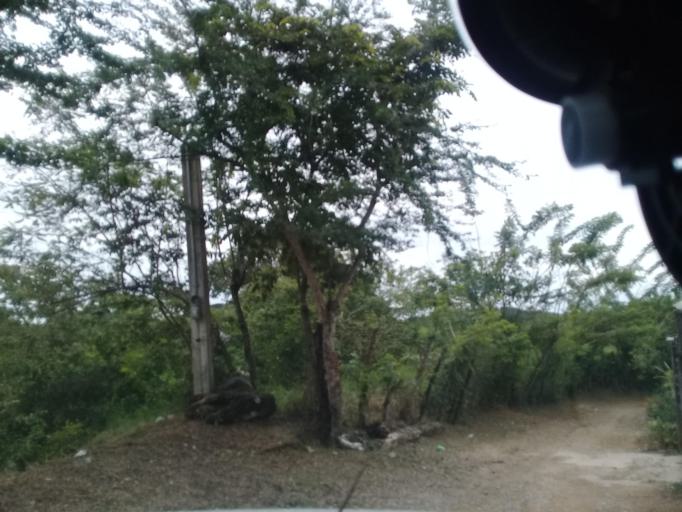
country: MX
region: Hidalgo
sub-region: Huejutla de Reyes
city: Parque de Poblamiento Solidaridad
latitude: 21.1797
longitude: -98.3908
